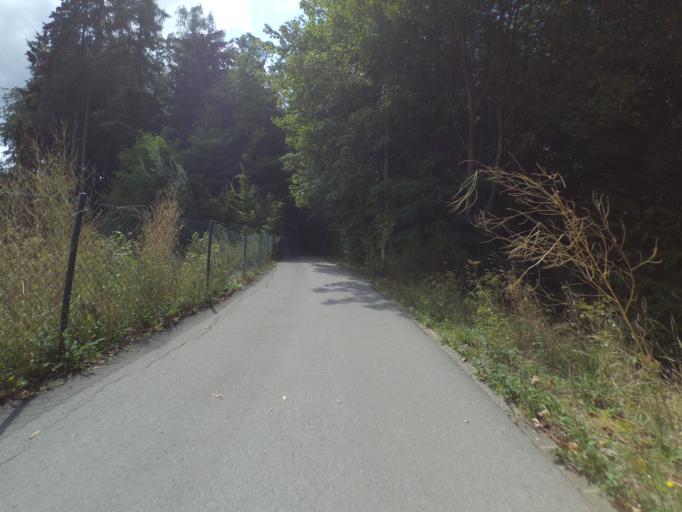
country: LU
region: Grevenmacher
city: Gonderange
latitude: 49.6652
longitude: 6.2289
